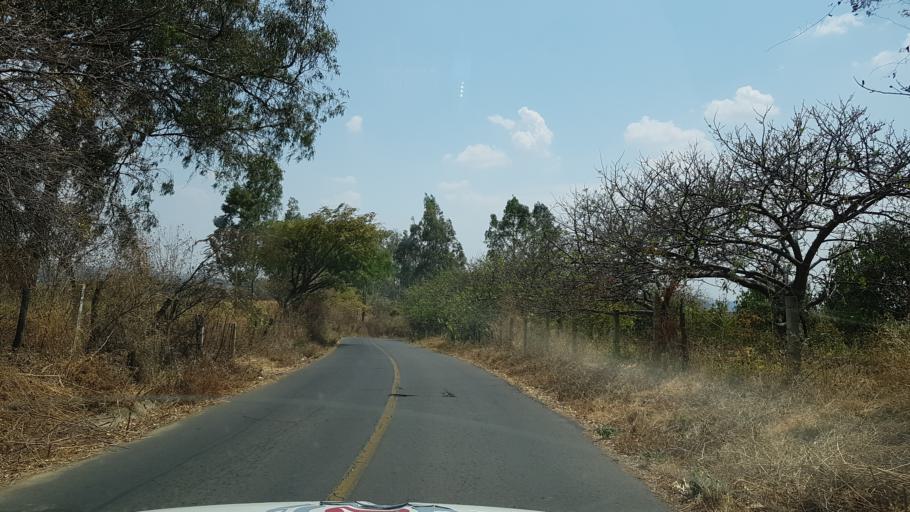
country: MX
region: Morelos
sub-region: Yecapixtla
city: Texcala
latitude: 18.9029
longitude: -98.8095
